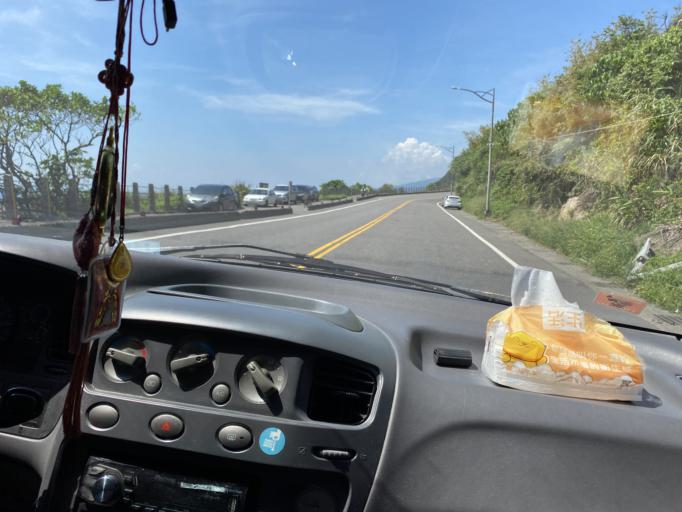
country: TW
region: Taiwan
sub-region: Keelung
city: Keelung
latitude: 24.9935
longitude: 121.9831
